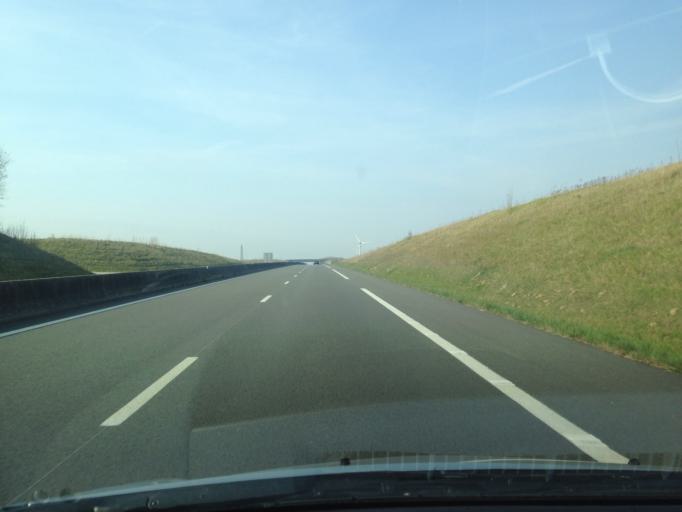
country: FR
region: Picardie
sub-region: Departement de la Somme
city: Rue
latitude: 50.2796
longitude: 1.7335
